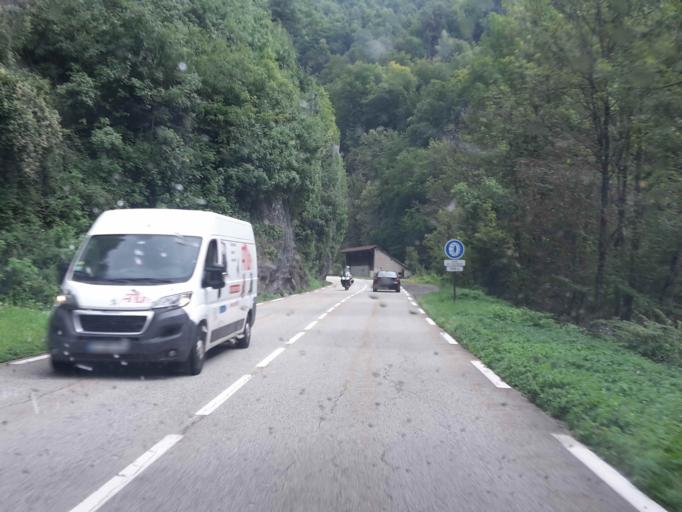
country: FR
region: Rhone-Alpes
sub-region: Departement de la Savoie
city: Ugine
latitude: 45.7514
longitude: 6.4379
